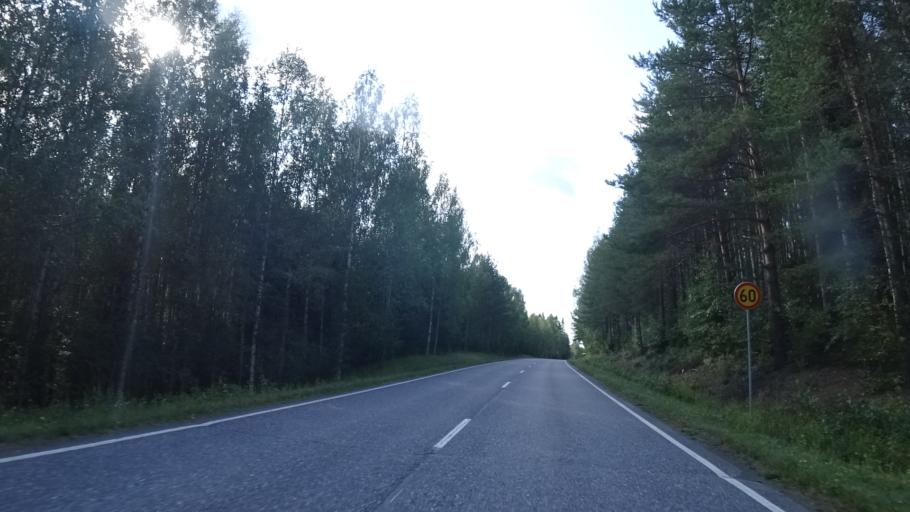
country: FI
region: North Karelia
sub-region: Keski-Karjala
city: Kitee
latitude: 62.0892
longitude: 30.1280
